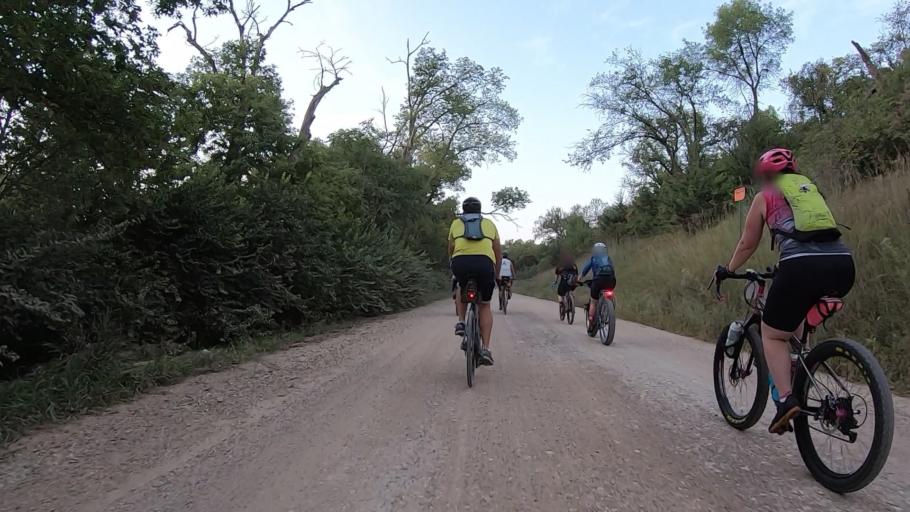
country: US
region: Kansas
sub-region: Marshall County
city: Marysville
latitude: 39.8339
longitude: -96.6652
